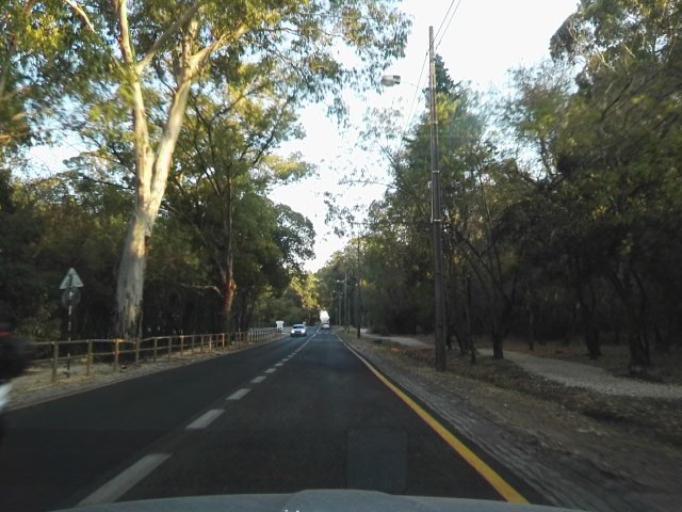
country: PT
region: Setubal
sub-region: Almada
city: Pragal
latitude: 38.7187
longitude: -9.1848
